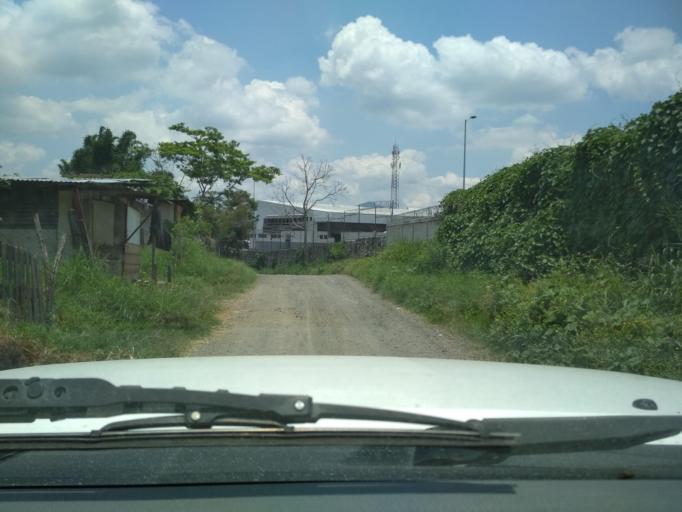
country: MX
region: Veracruz
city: Cordoba
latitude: 18.8847
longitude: -96.9184
